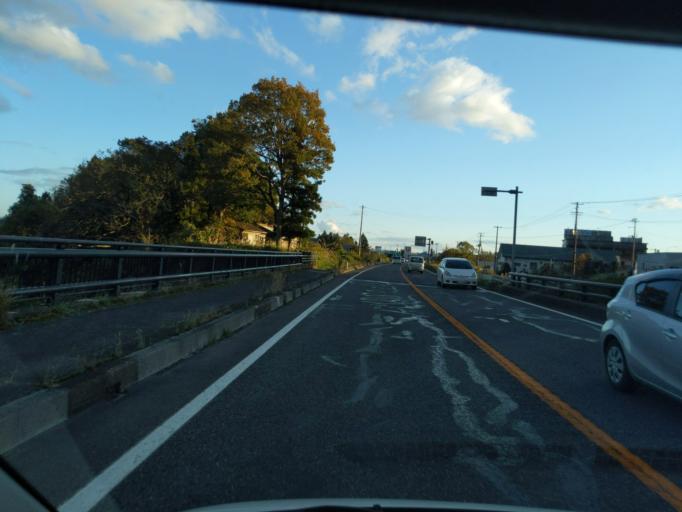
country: JP
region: Iwate
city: Mizusawa
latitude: 39.2051
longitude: 141.1089
